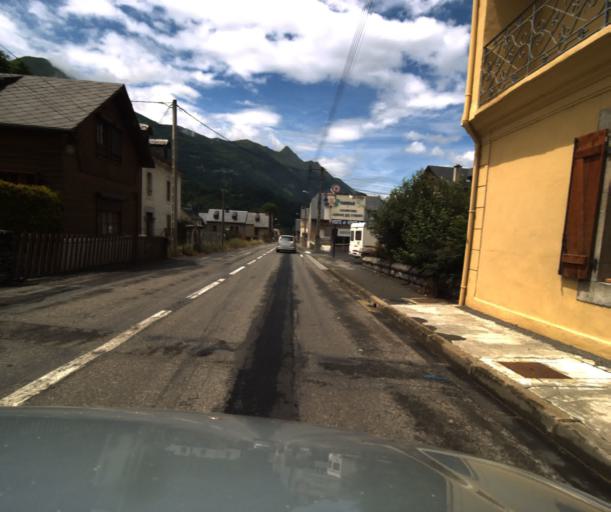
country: FR
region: Midi-Pyrenees
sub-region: Departement des Hautes-Pyrenees
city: Luz-Saint-Sauveur
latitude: 42.8781
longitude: -0.0086
